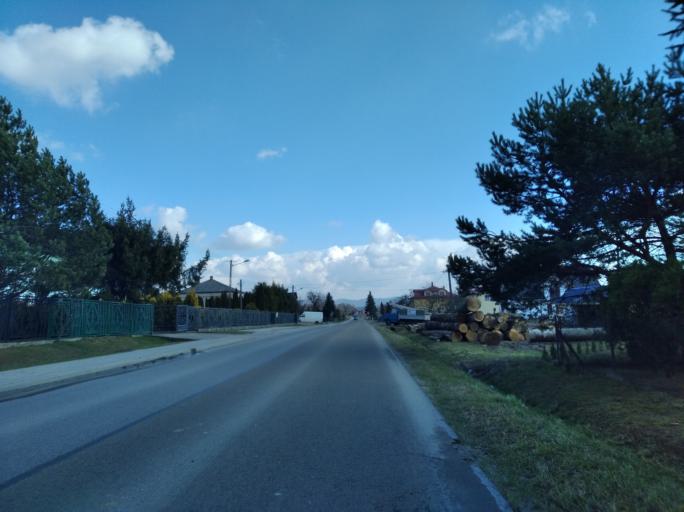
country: PL
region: Subcarpathian Voivodeship
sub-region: Powiat strzyzowski
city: Frysztak
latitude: 49.8486
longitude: 21.5429
